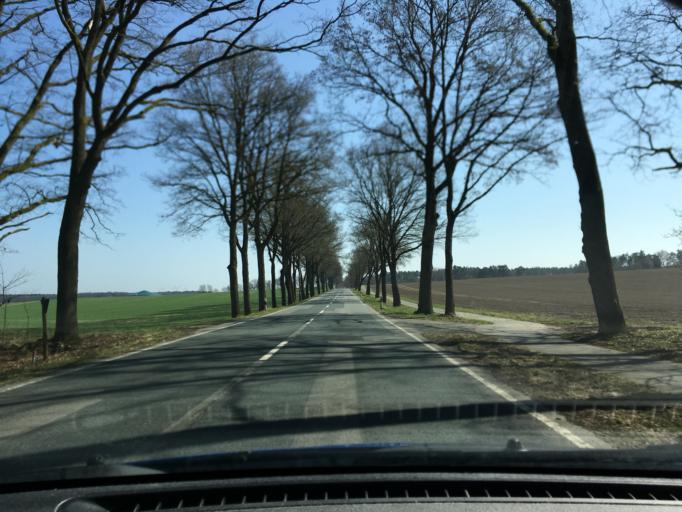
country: DE
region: Lower Saxony
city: Rehlingen
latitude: 53.0856
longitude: 10.2730
